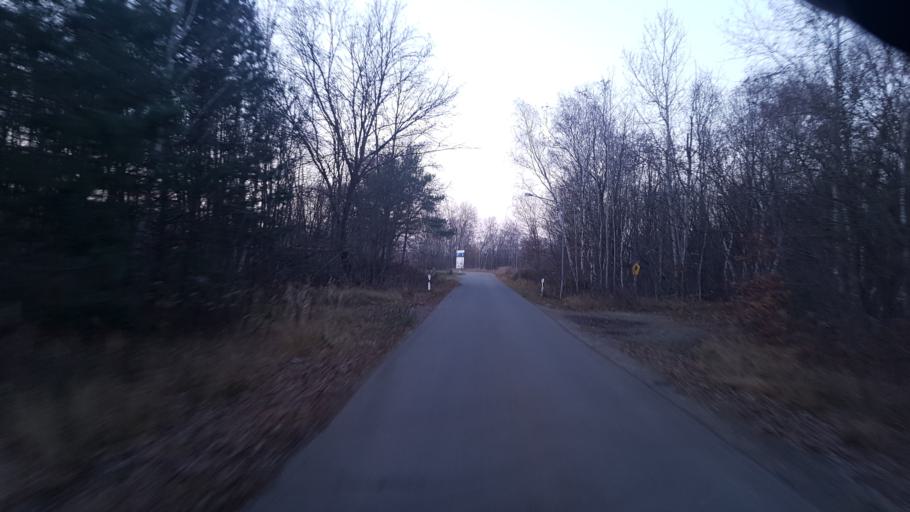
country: DE
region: Brandenburg
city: Lauchhammer
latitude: 51.5211
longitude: 13.7381
